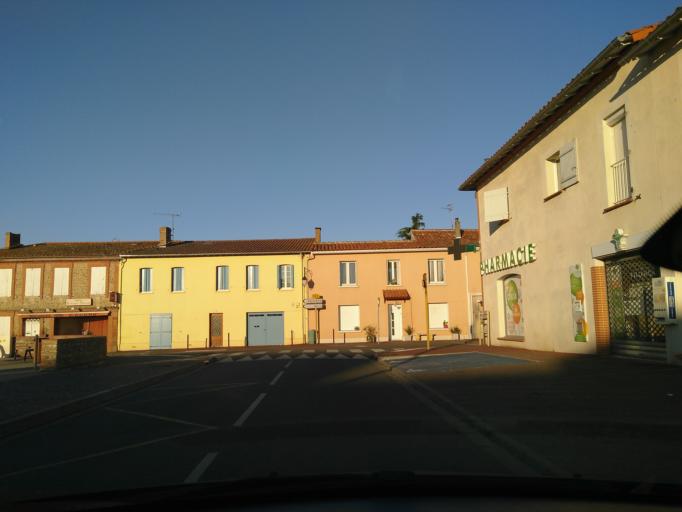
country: FR
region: Midi-Pyrenees
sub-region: Departement de la Haute-Garonne
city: Merville
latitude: 43.7215
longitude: 1.2976
